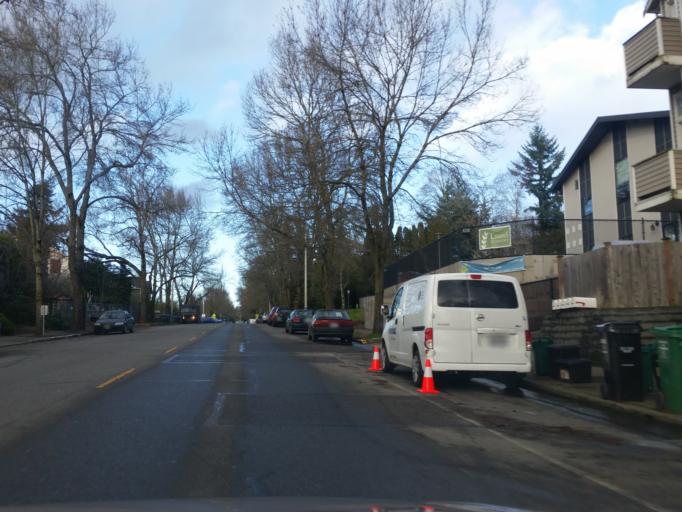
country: US
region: Washington
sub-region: King County
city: Lake Forest Park
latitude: 47.7208
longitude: -122.2908
